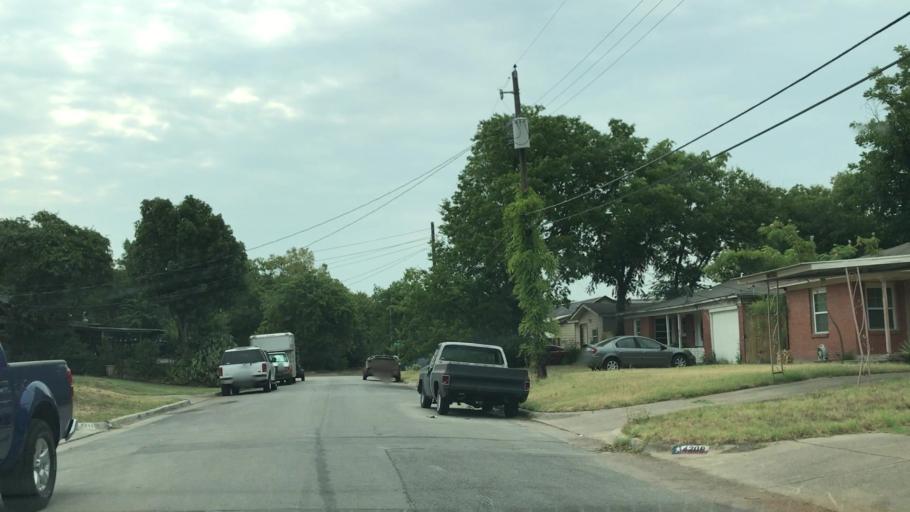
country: US
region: Texas
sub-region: Tarrant County
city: Haltom City
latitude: 32.7662
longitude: -97.2855
